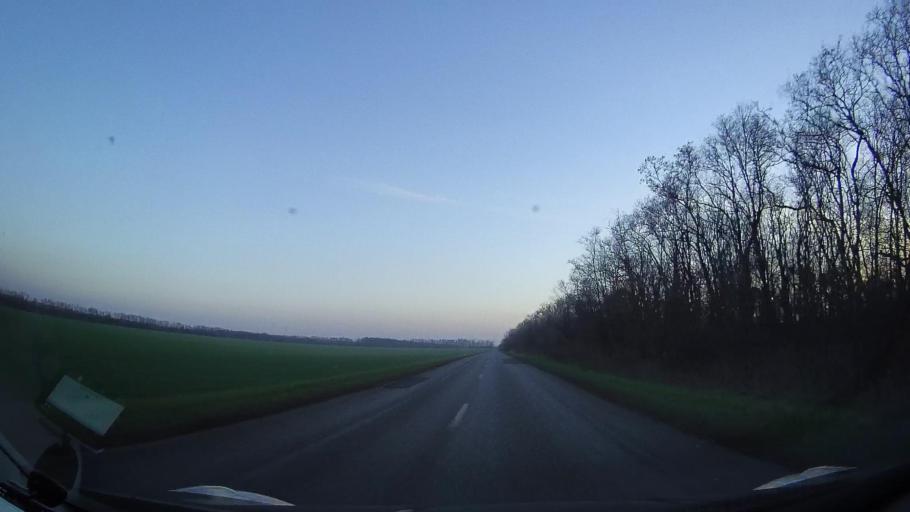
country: RU
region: Rostov
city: Zernograd
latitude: 46.9743
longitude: 40.3915
